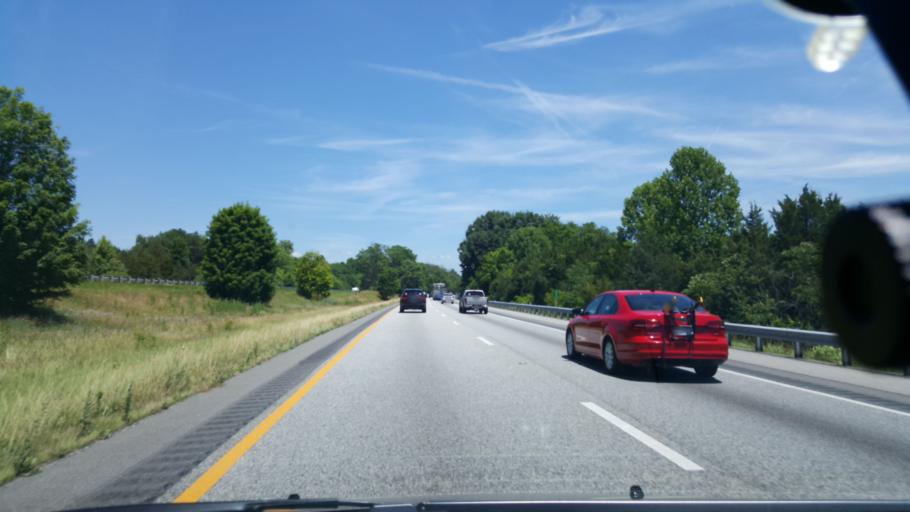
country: US
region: Virginia
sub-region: Botetourt County
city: Daleville
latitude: 37.4393
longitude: -79.8673
